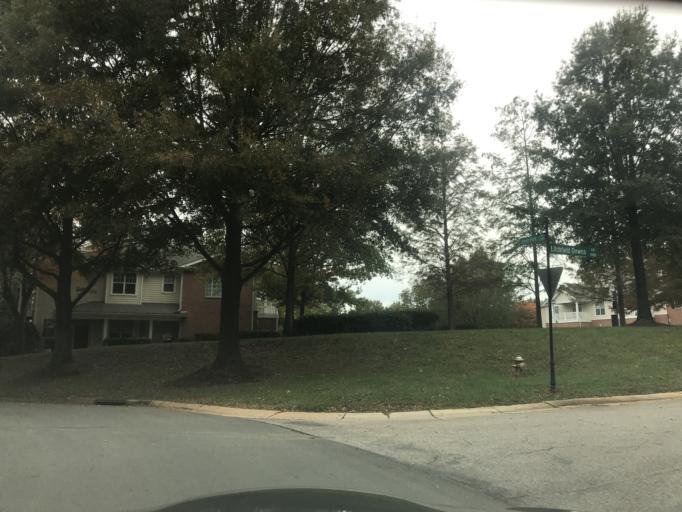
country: US
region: North Carolina
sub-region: Wake County
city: West Raleigh
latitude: 35.8455
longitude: -78.6695
